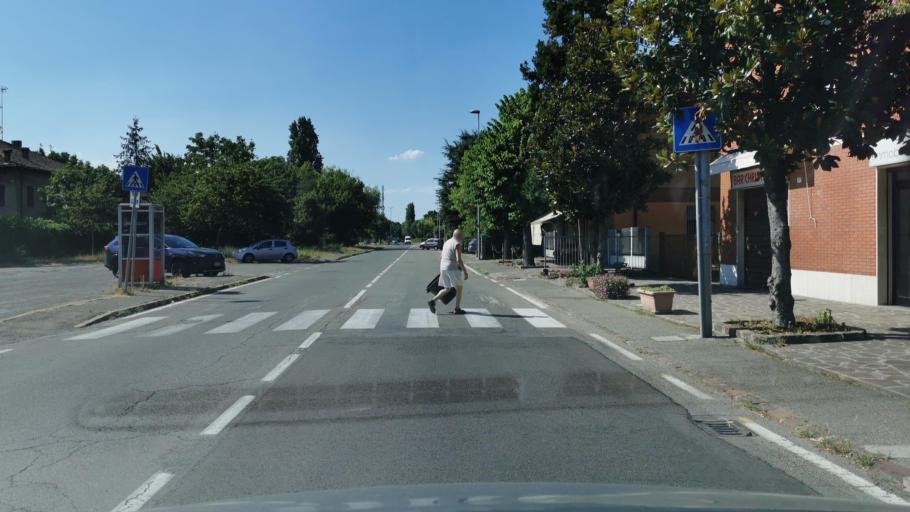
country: IT
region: Emilia-Romagna
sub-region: Provincia di Modena
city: Modena
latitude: 44.6194
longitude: 10.9306
